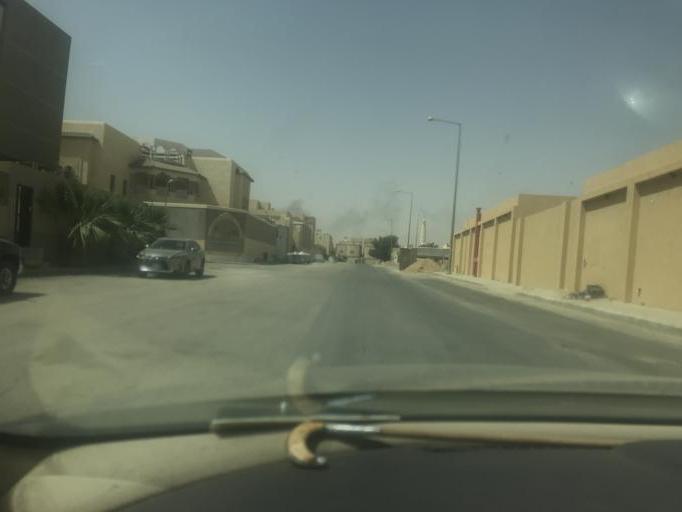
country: SA
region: Ar Riyad
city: Riyadh
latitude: 24.8219
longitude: 46.6056
